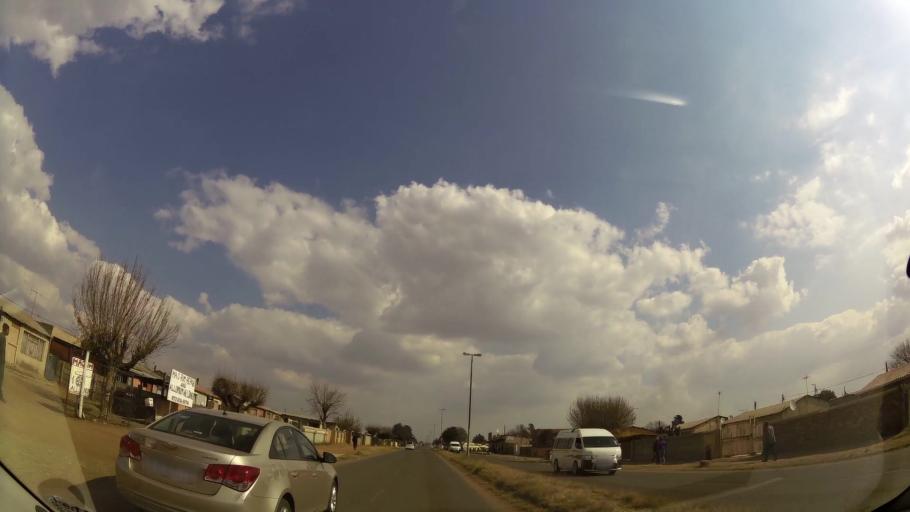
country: ZA
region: Gauteng
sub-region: Ekurhuleni Metropolitan Municipality
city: Springs
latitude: -26.1270
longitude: 28.4454
